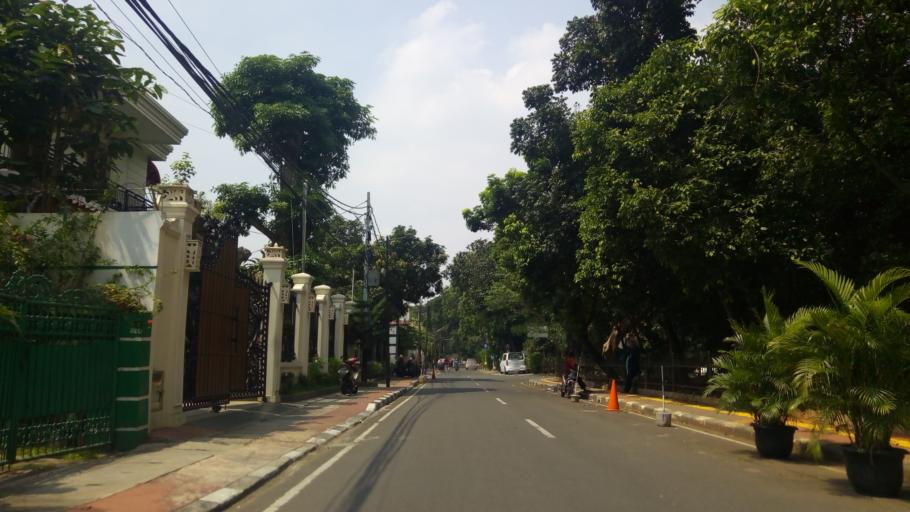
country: ID
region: Jakarta Raya
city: Jakarta
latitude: -6.1999
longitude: 106.8255
